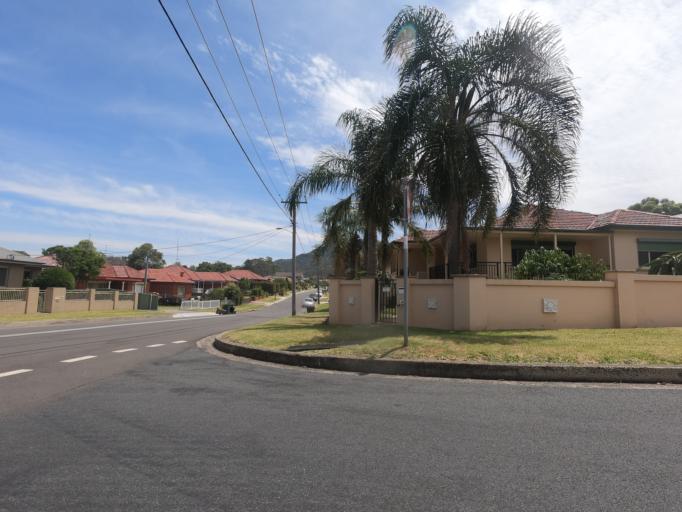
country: AU
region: New South Wales
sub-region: Wollongong
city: Fairy Meadow
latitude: -34.3934
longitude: 150.8877
